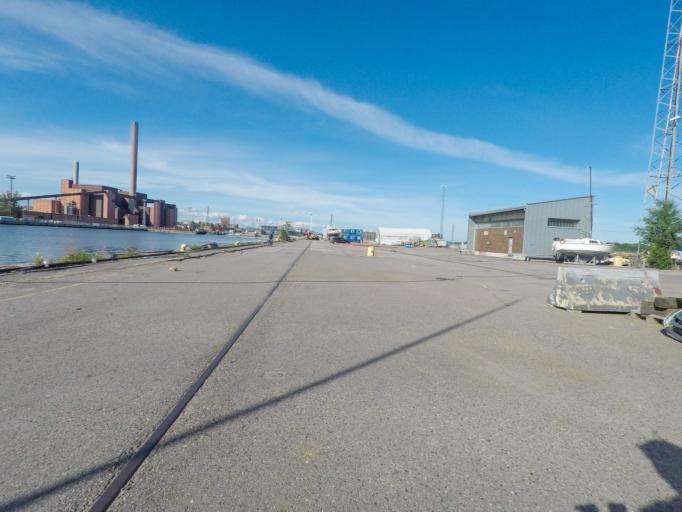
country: FI
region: Uusimaa
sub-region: Helsinki
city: Helsinki
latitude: 60.1785
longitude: 24.9709
